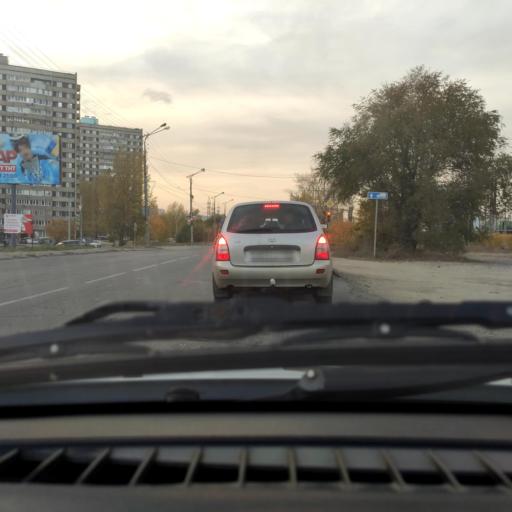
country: RU
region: Samara
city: Zhigulevsk
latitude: 53.4773
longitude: 49.5237
